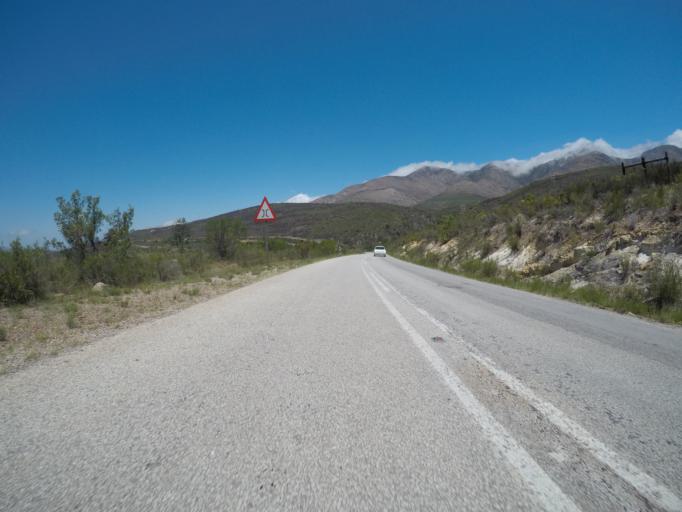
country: ZA
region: Eastern Cape
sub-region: Cacadu District Municipality
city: Kareedouw
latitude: -33.8921
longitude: 24.1020
